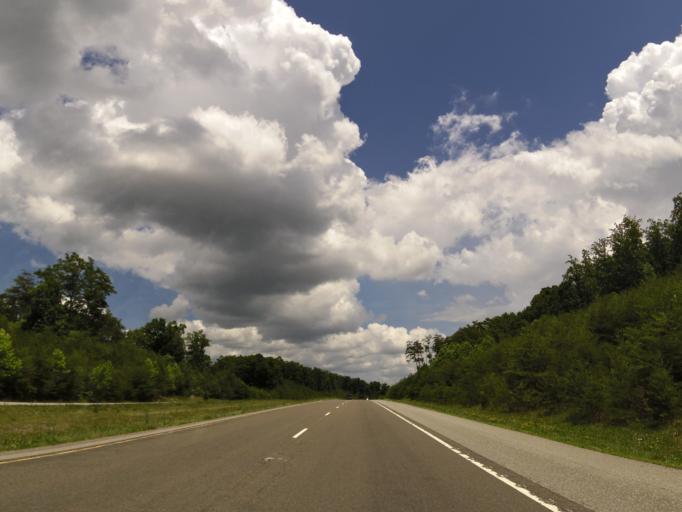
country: US
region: Tennessee
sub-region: Claiborne County
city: Harrogate
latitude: 36.6021
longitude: -83.6521
